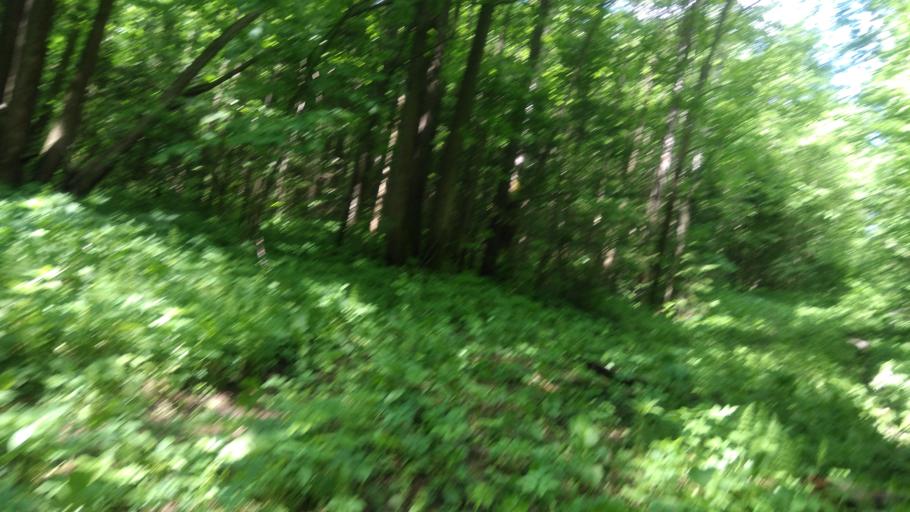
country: RU
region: Perm
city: Ferma
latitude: 57.9651
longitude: 56.3436
